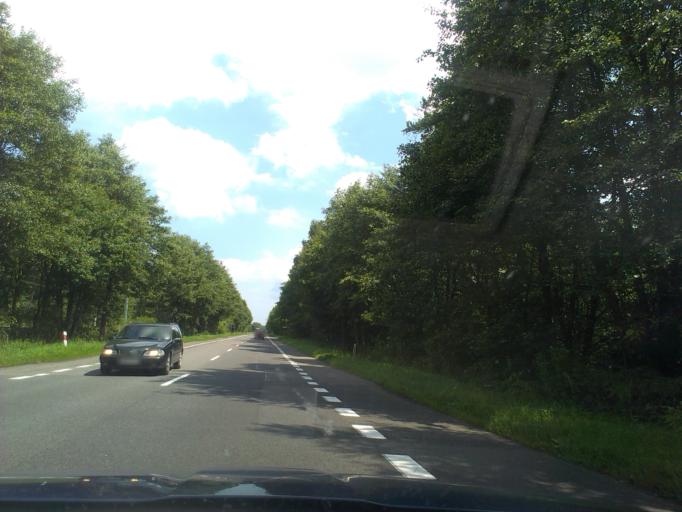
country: PL
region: West Pomeranian Voivodeship
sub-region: Powiat kamienski
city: Miedzyzdroje
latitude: 53.9066
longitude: 14.3869
